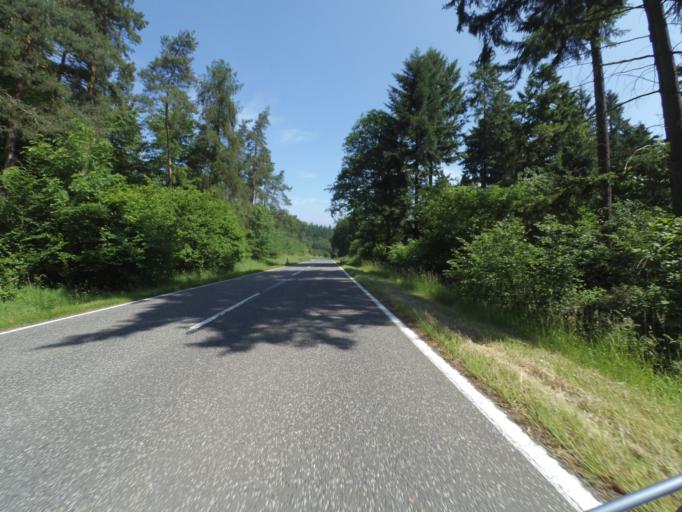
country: DE
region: Rheinland-Pfalz
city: Filsen
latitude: 50.2211
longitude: 7.5579
